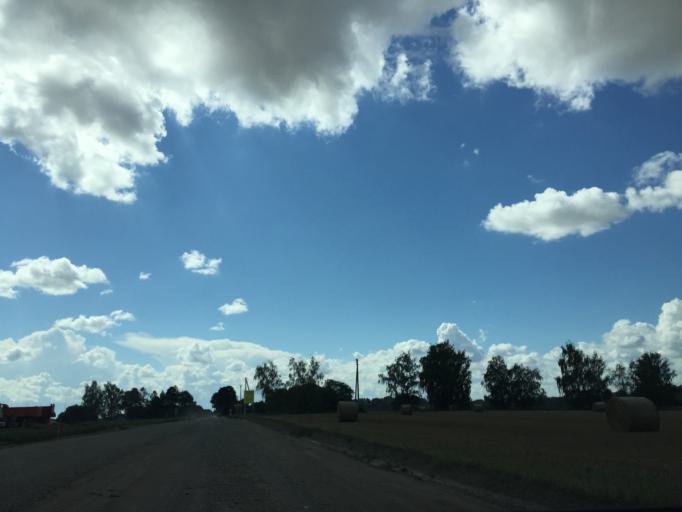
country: LV
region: Rundales
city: Pilsrundale
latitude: 56.3013
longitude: 24.0000
